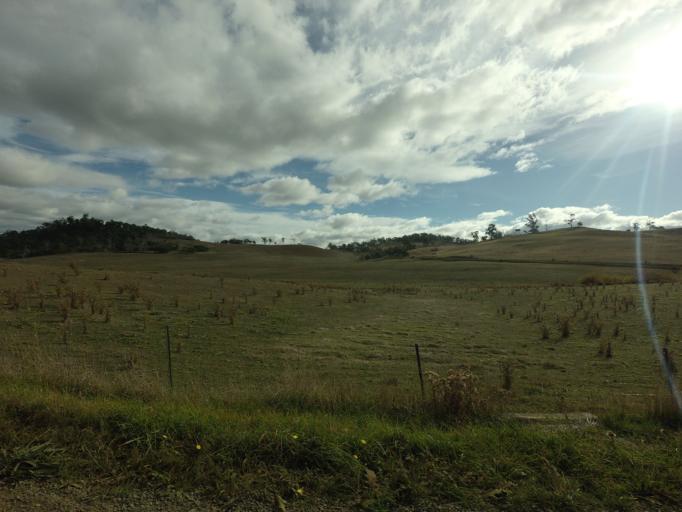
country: AU
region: Tasmania
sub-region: Brighton
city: Bridgewater
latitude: -42.4619
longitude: 147.2777
